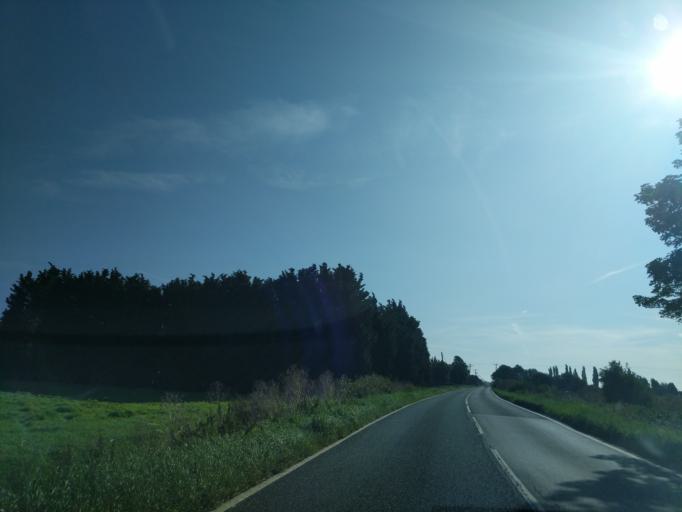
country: GB
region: England
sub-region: Lincolnshire
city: Bourne
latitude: 52.7722
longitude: -0.3453
